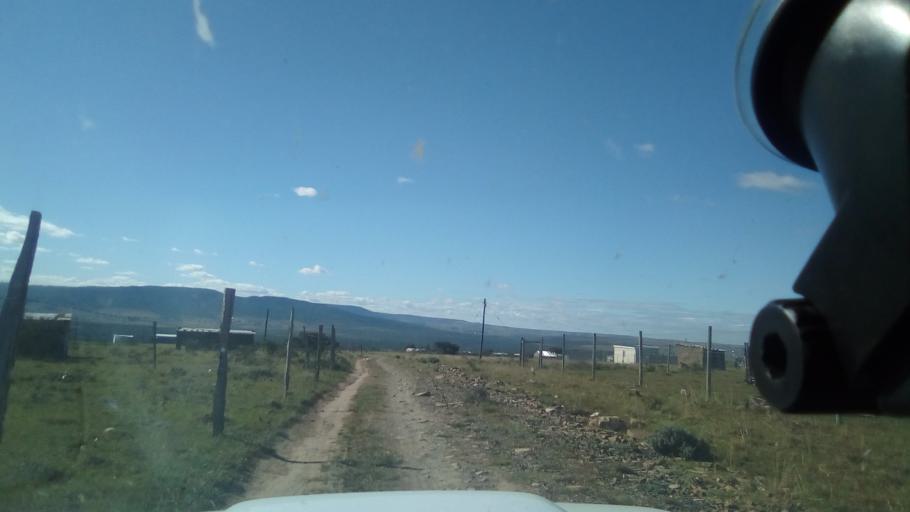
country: ZA
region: Eastern Cape
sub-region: Buffalo City Metropolitan Municipality
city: Bhisho
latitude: -32.7815
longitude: 27.3334
